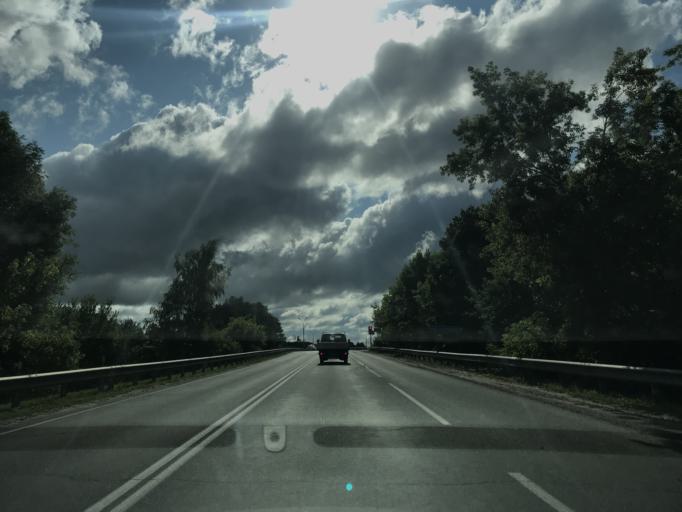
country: BY
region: Minsk
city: Borovlyany
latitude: 53.9671
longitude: 27.6399
